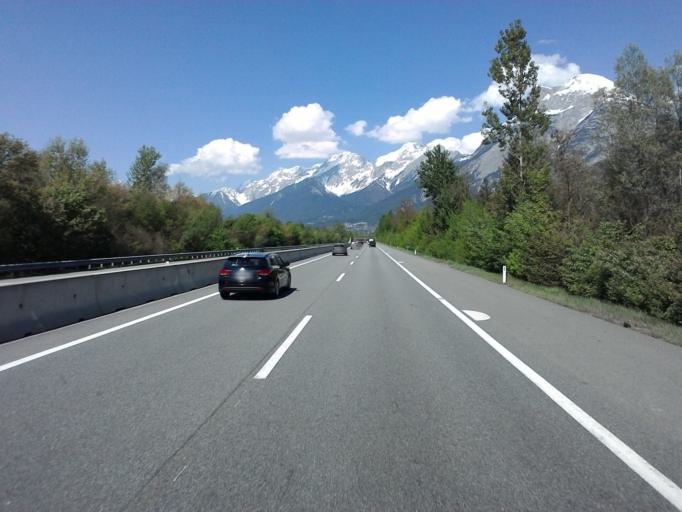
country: AT
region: Tyrol
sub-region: Politischer Bezirk Innsbruck Land
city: Pettnau
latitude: 47.2943
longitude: 11.1409
